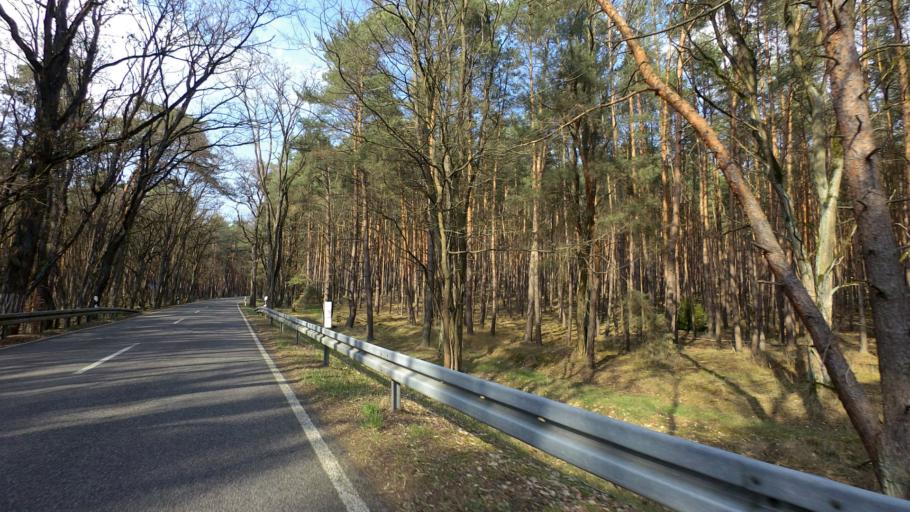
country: DE
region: Brandenburg
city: Dahme
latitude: 51.9353
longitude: 13.4472
